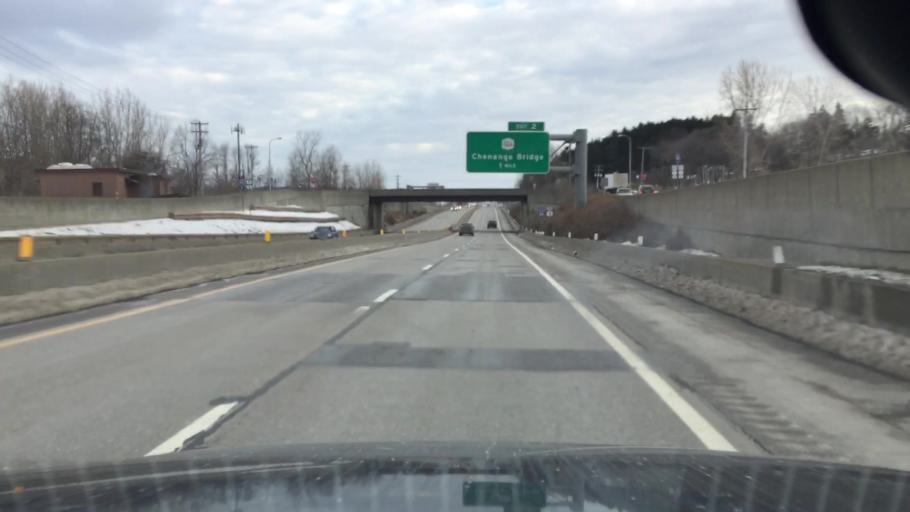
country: US
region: New York
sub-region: Broome County
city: Port Dickinson
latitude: 42.1516
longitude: -75.8891
